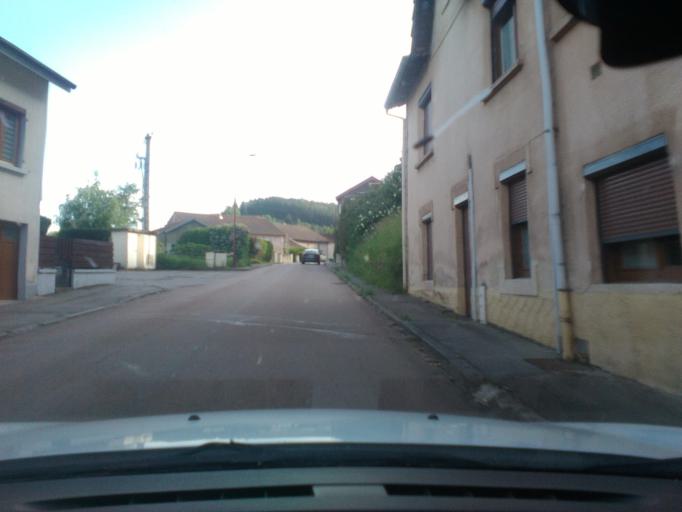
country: FR
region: Lorraine
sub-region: Departement des Vosges
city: Bruyeres
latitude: 48.2404
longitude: 6.7322
